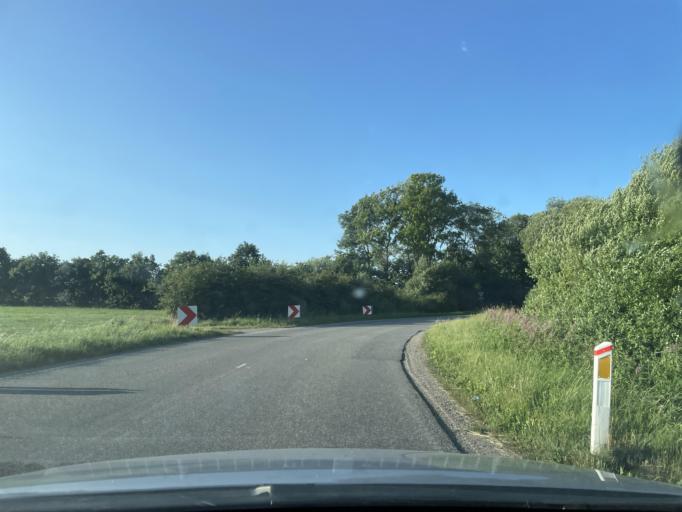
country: DK
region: South Denmark
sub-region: Tonder Kommune
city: Toftlund
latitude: 55.0673
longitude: 9.1564
